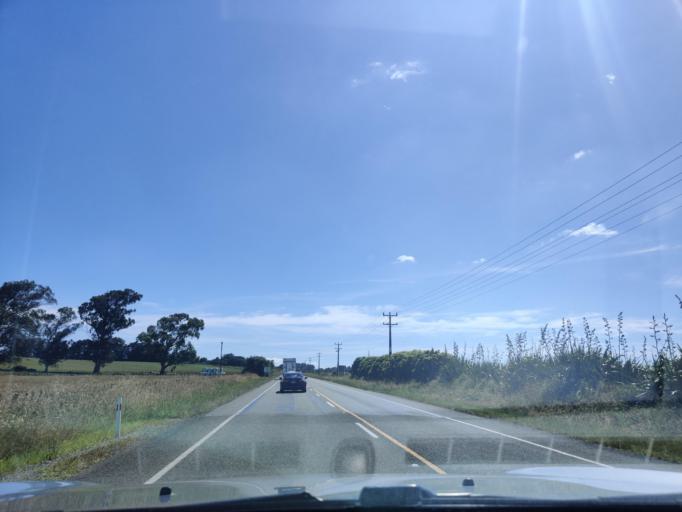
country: NZ
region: Manawatu-Wanganui
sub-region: Rangitikei District
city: Bulls
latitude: -40.0688
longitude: 175.4192
